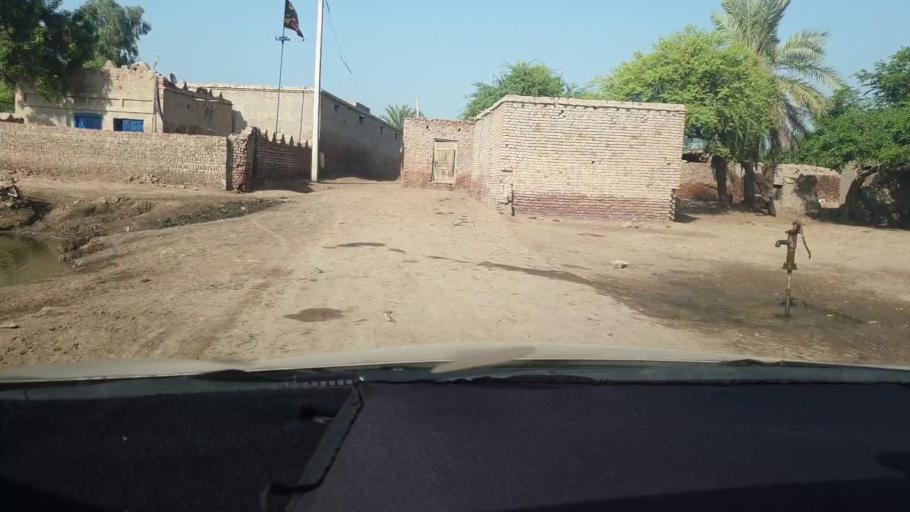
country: PK
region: Sindh
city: Miro Khan
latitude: 27.7520
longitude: 68.1500
